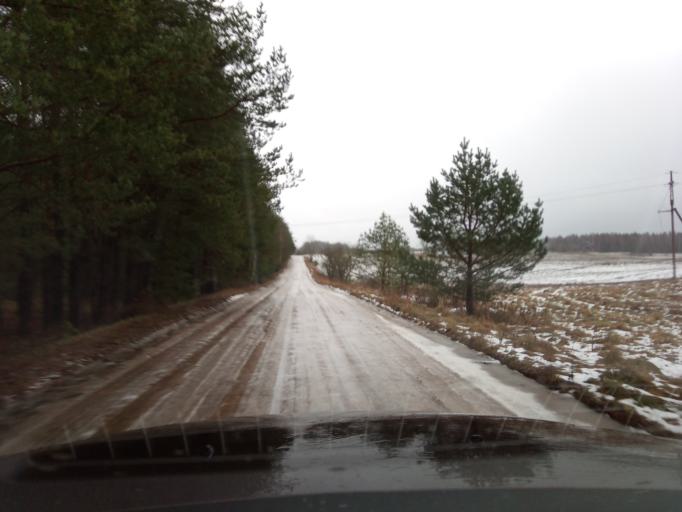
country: LT
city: Svencioneliai
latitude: 55.3457
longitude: 25.8339
